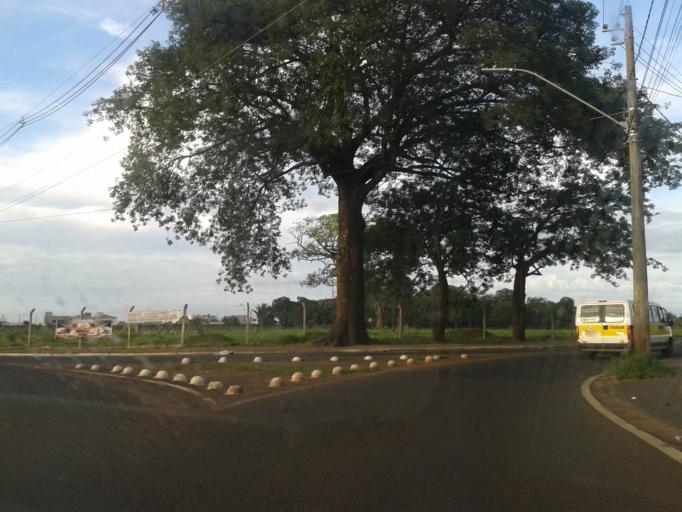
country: BR
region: Minas Gerais
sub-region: Araguari
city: Araguari
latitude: -18.6429
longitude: -48.2109
